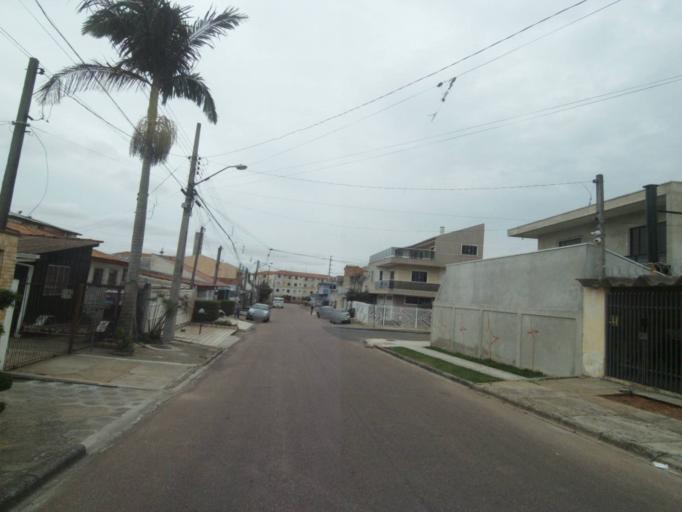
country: BR
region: Parana
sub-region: Sao Jose Dos Pinhais
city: Sao Jose dos Pinhais
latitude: -25.5479
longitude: -49.2677
